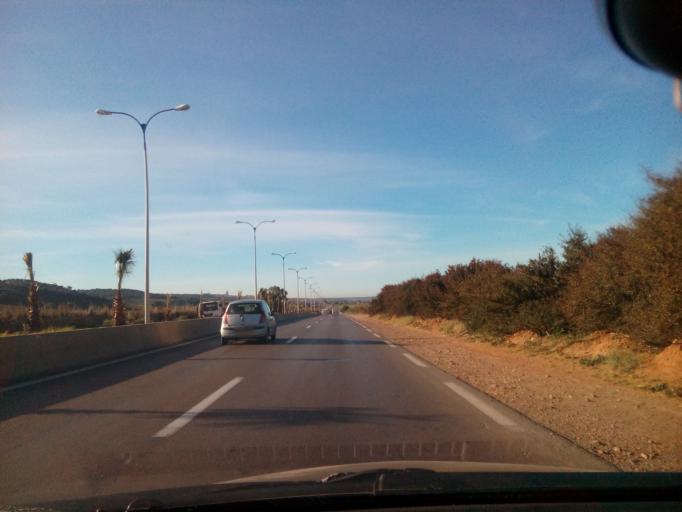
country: DZ
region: Mostaganem
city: Mostaganem
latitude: 35.8459
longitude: 0.0167
